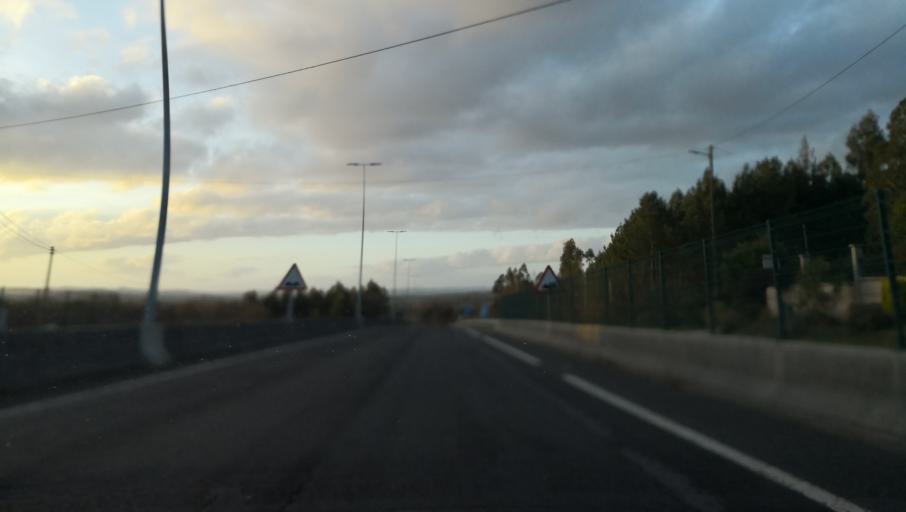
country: ES
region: Galicia
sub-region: Provincia da Coruna
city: Oroso
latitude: 42.9051
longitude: -8.4283
